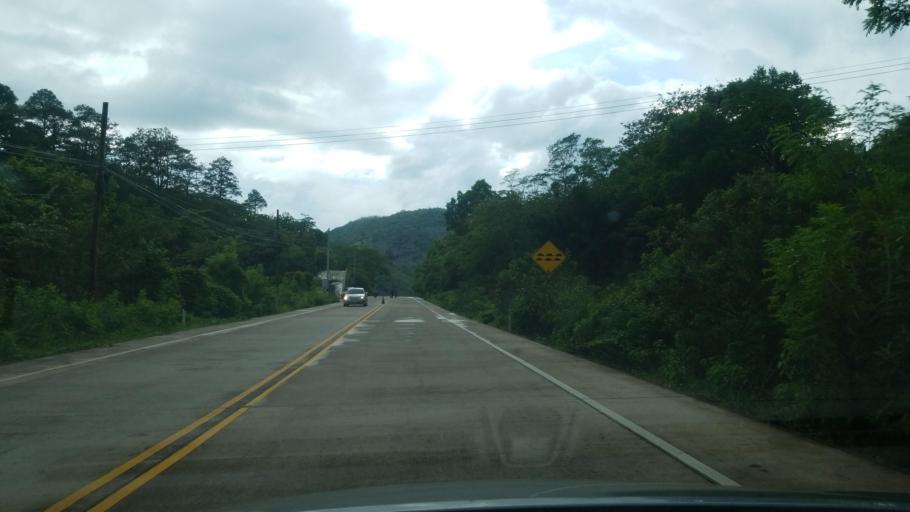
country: HN
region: Copan
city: Copan
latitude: 14.8472
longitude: -89.1911
